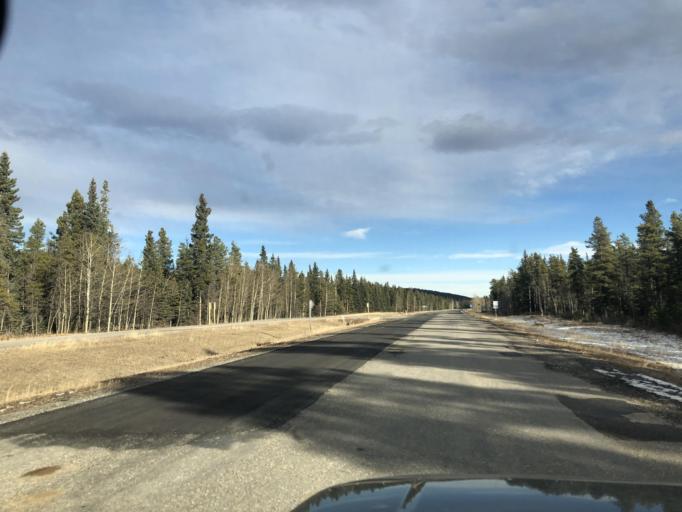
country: CA
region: Alberta
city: Cochrane
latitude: 51.0424
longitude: -114.8624
